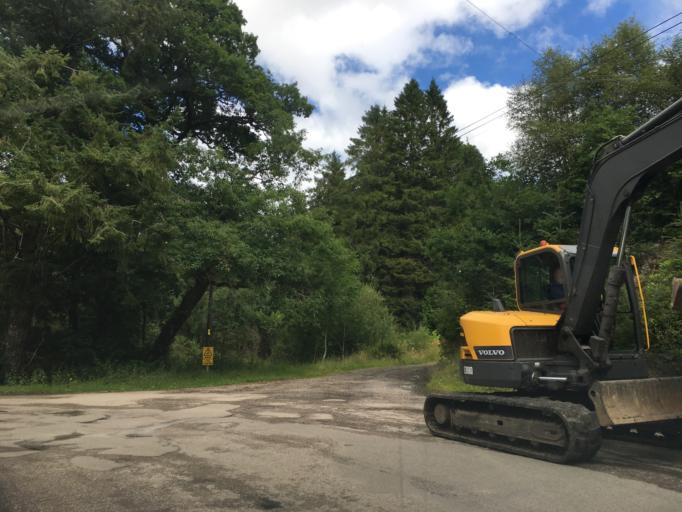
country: GB
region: Scotland
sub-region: Argyll and Bute
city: Oban
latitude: 56.2750
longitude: -5.2780
